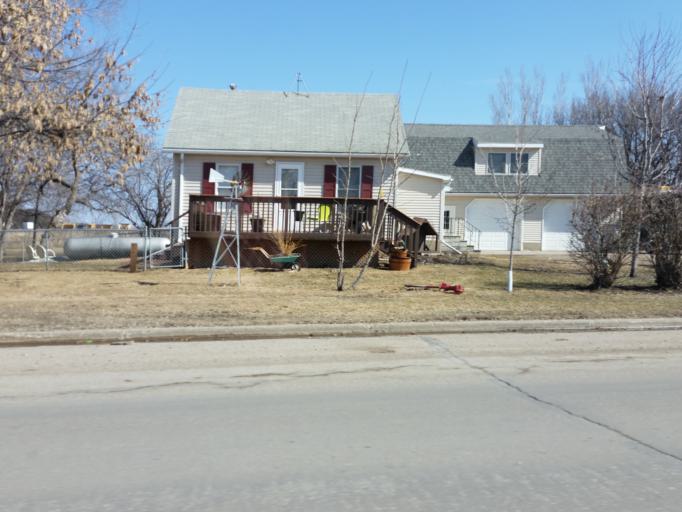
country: US
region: North Dakota
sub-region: Walsh County
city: Grafton
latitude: 48.2943
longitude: -97.3715
